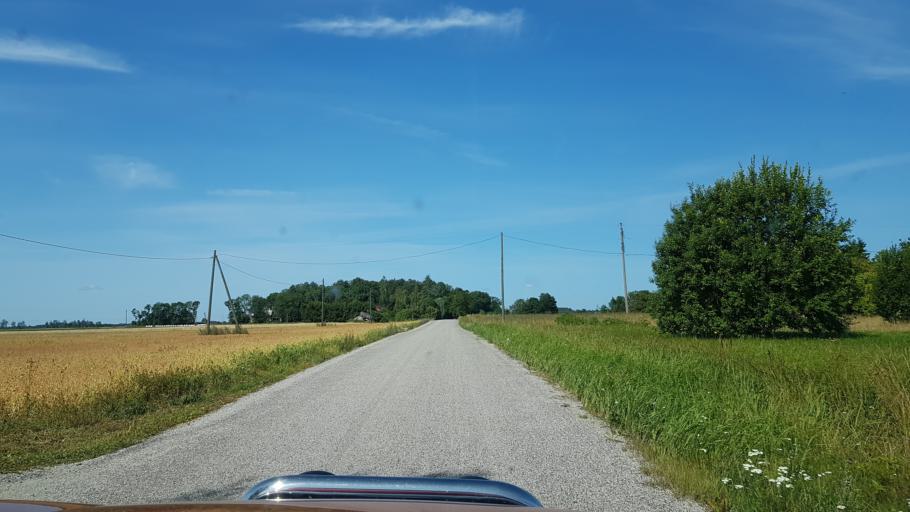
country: EE
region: Jaervamaa
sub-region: Jaerva-Jaani vald
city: Jarva-Jaani
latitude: 59.0876
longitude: 25.7378
